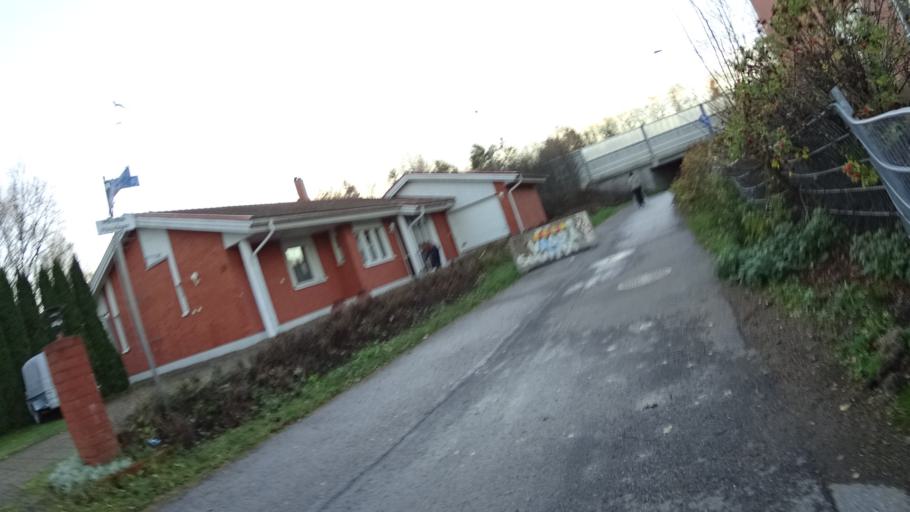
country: FI
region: Uusimaa
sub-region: Helsinki
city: Helsinki
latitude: 60.2487
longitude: 24.9494
